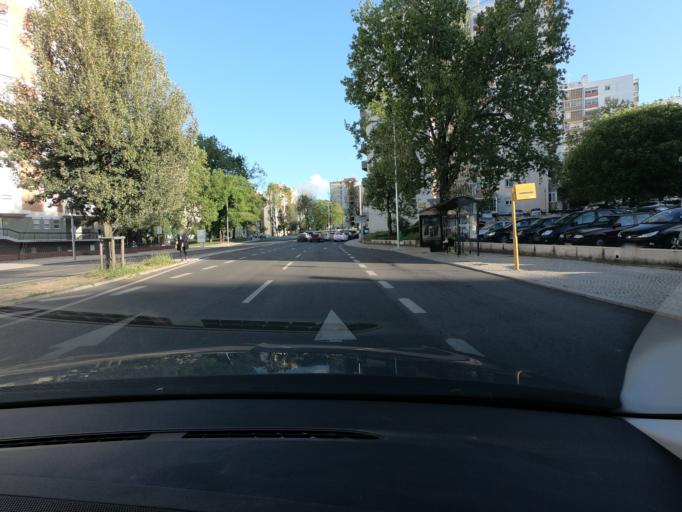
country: PT
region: Lisbon
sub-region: Loures
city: Moscavide
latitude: 38.7643
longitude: -9.1190
